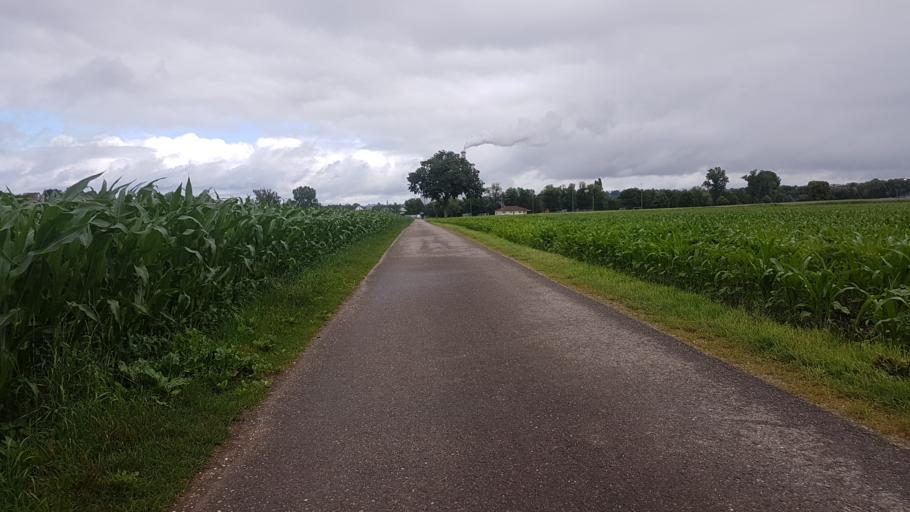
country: DE
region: Baden-Wuerttemberg
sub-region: Tuebingen Region
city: Dettingen
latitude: 48.2569
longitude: 9.7244
